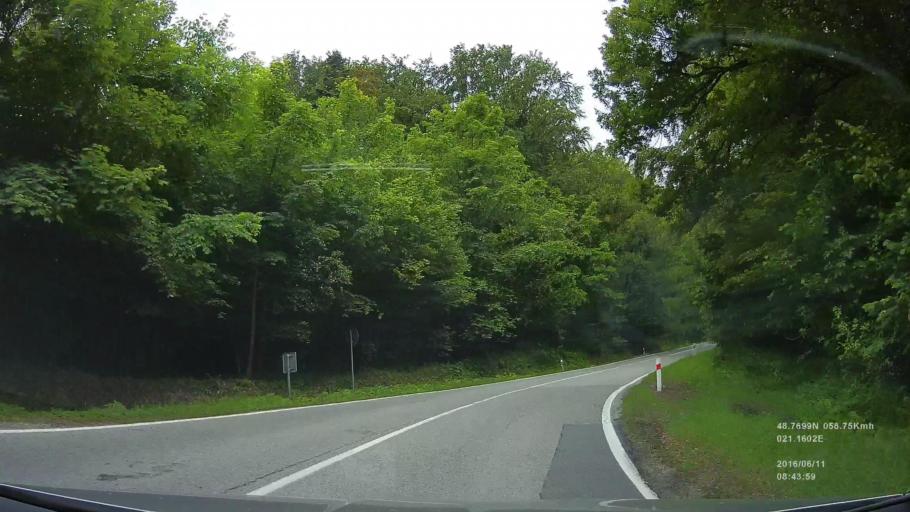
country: SK
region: Kosicky
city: Kosice
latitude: 48.7516
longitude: 21.2072
